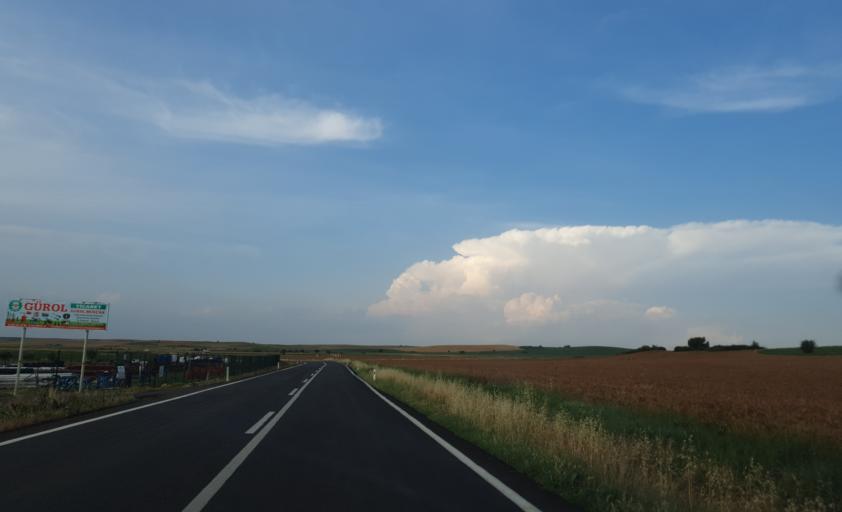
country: TR
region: Tekirdag
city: Hayrabolu
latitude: 41.2378
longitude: 27.1312
